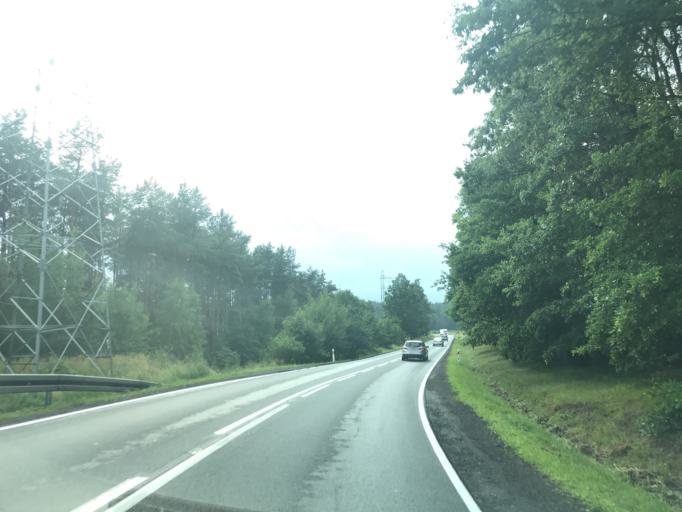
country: PL
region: Pomeranian Voivodeship
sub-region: Powiat czluchowski
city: Przechlewo
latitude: 53.7304
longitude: 17.2213
